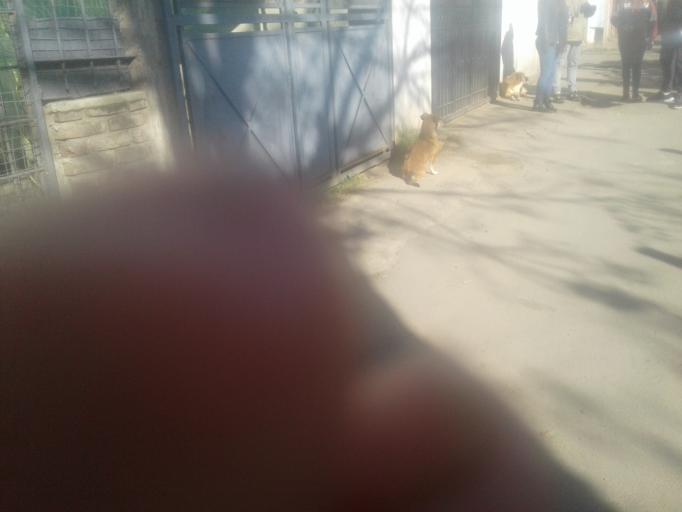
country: AR
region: Buenos Aires F.D.
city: Villa Lugano
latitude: -34.6724
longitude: -58.4676
